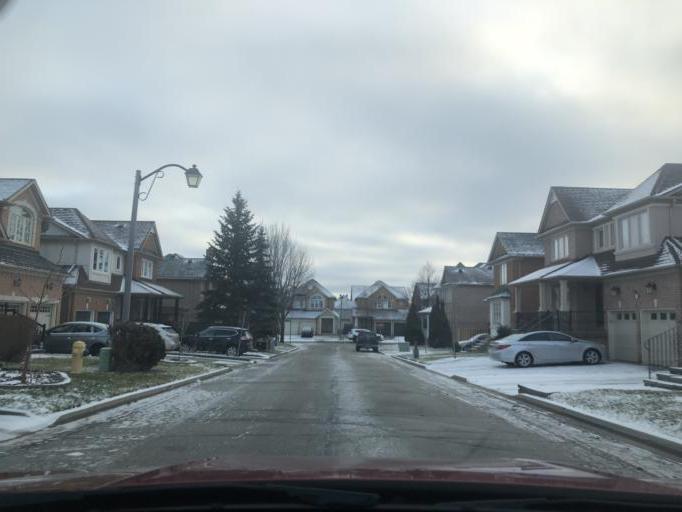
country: CA
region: Ontario
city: Markham
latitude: 43.8667
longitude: -79.2363
